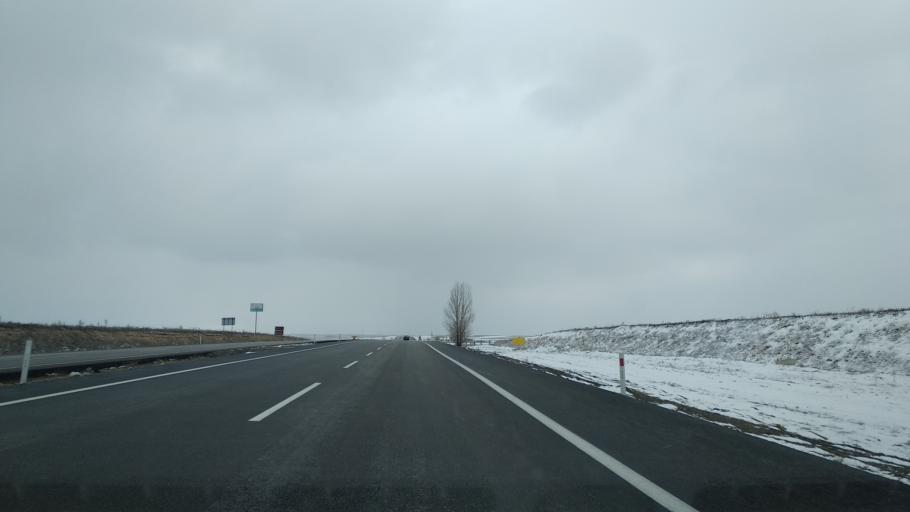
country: TR
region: Kayseri
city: Elbasi
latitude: 38.6503
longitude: 35.9877
